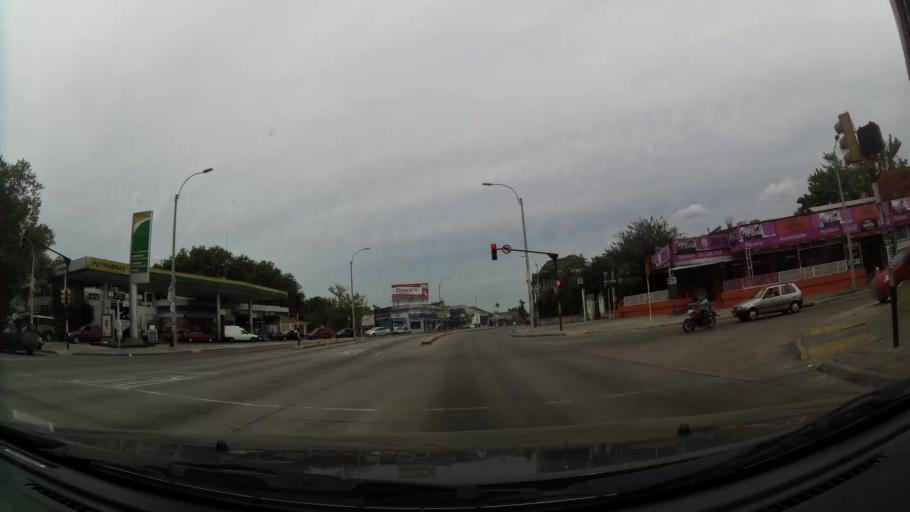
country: UY
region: Canelones
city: La Paz
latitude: -34.8065
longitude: -56.2220
